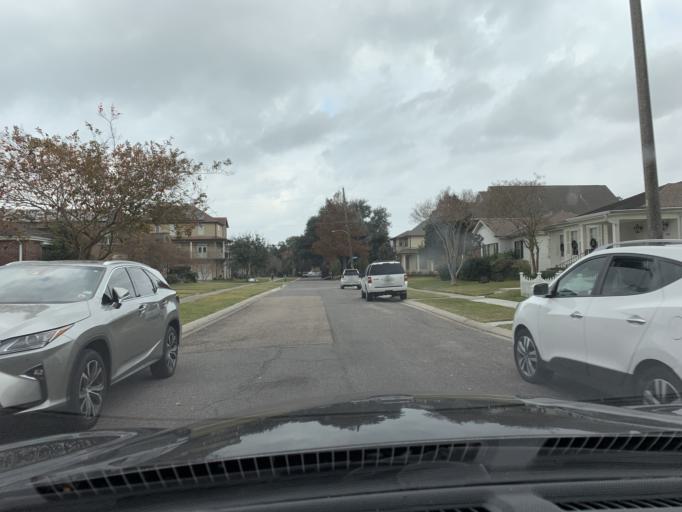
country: US
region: Louisiana
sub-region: Jefferson Parish
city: Metairie
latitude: 30.0073
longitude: -90.1012
